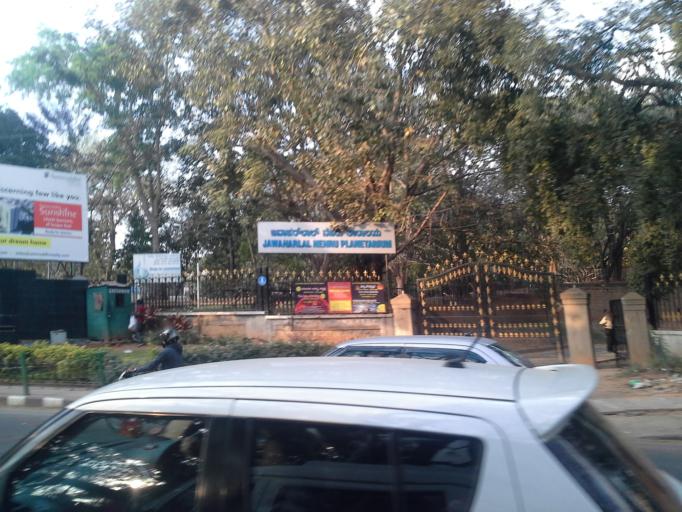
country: IN
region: Karnataka
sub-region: Bangalore Urban
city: Bangalore
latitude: 12.9846
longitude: 77.5890
